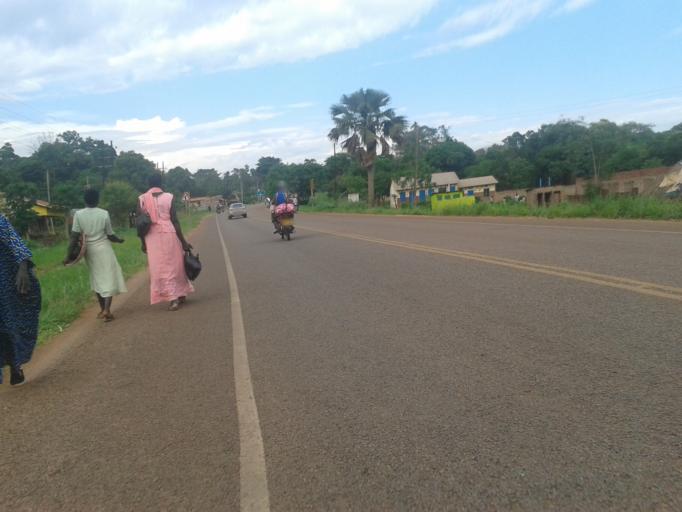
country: UG
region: Northern Region
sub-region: Gulu District
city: Gulu
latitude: 2.7621
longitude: 32.2761
